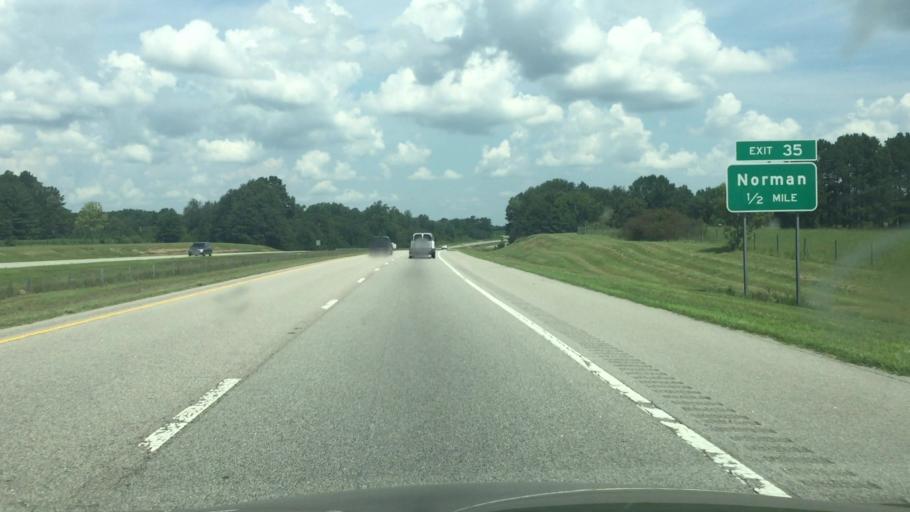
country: US
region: North Carolina
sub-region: Richmond County
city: Ellerbe
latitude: 35.1614
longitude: -79.7161
